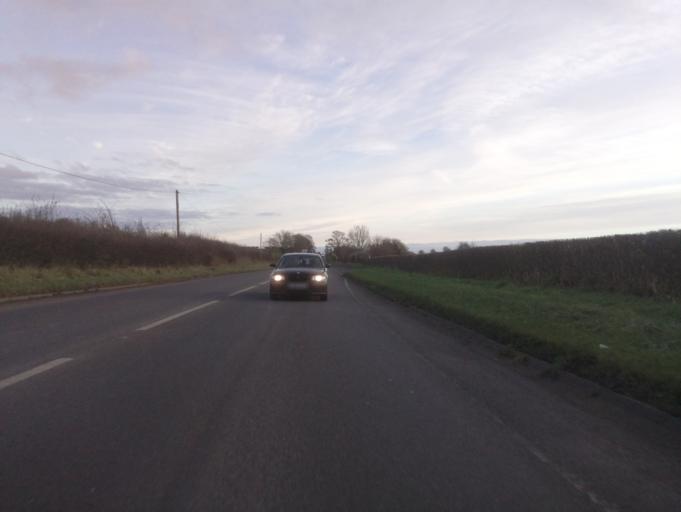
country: GB
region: England
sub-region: Staffordshire
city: Stone
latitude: 52.8786
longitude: -2.1073
